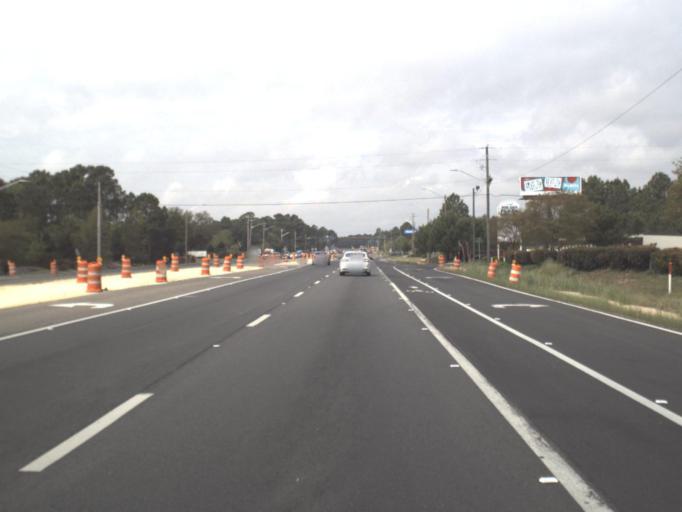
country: US
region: Florida
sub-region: Santa Rosa County
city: Navarre
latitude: 30.4098
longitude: -86.8265
